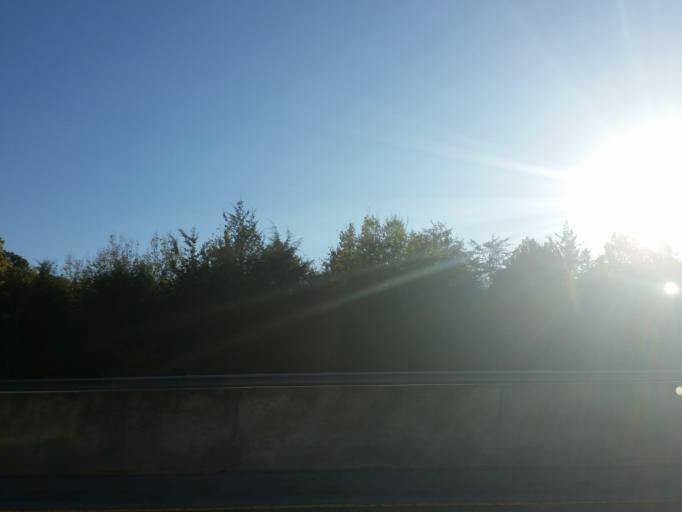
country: US
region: Tennessee
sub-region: Grainger County
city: Rutledge
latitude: 36.3491
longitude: -83.4327
